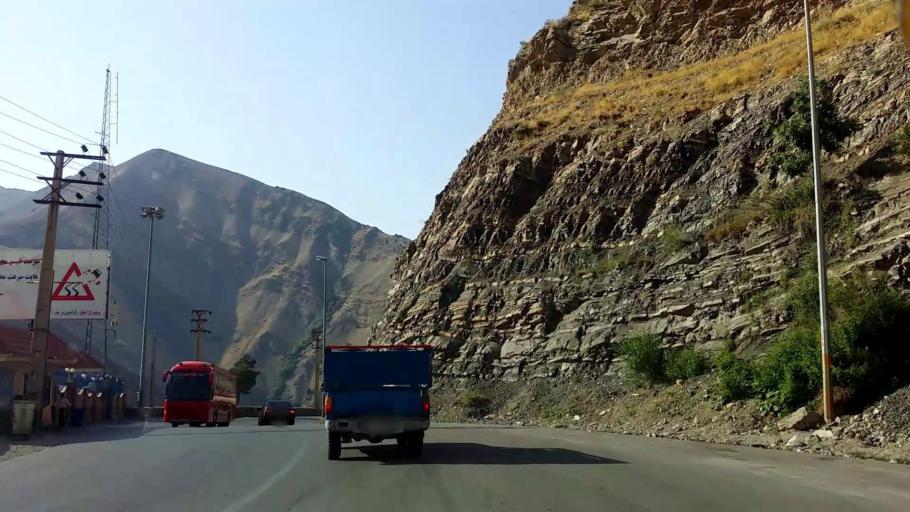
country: IR
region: Alborz
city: Karaj
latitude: 35.9552
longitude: 51.0855
